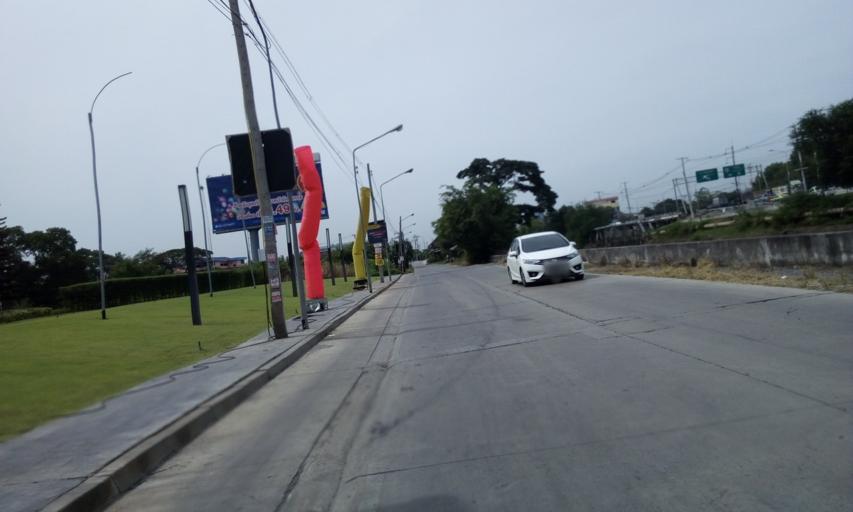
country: TH
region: Pathum Thani
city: Ban Rangsit
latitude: 14.0292
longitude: 100.7575
